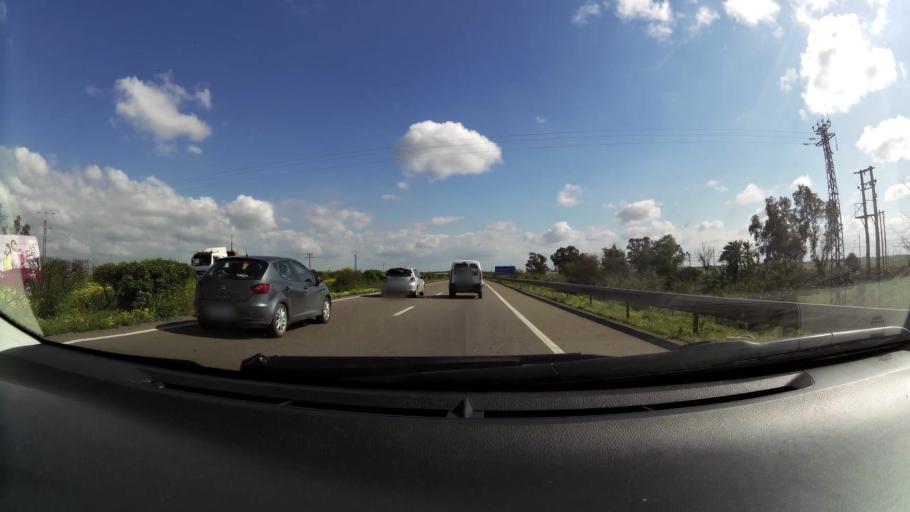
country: MA
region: Chaouia-Ouardigha
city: Nouaseur
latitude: 33.3630
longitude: -7.6197
